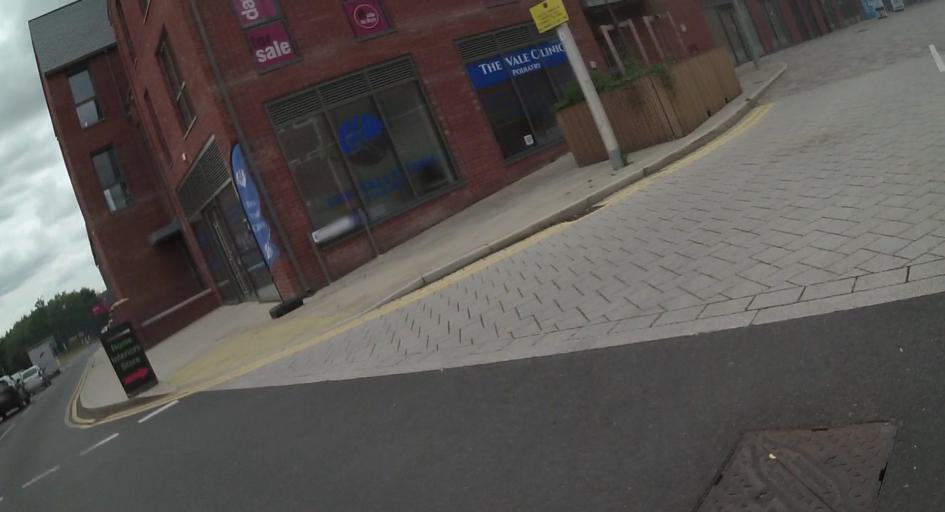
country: GB
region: England
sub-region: Wokingham
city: Wokingham
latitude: 51.4082
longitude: -0.8363
